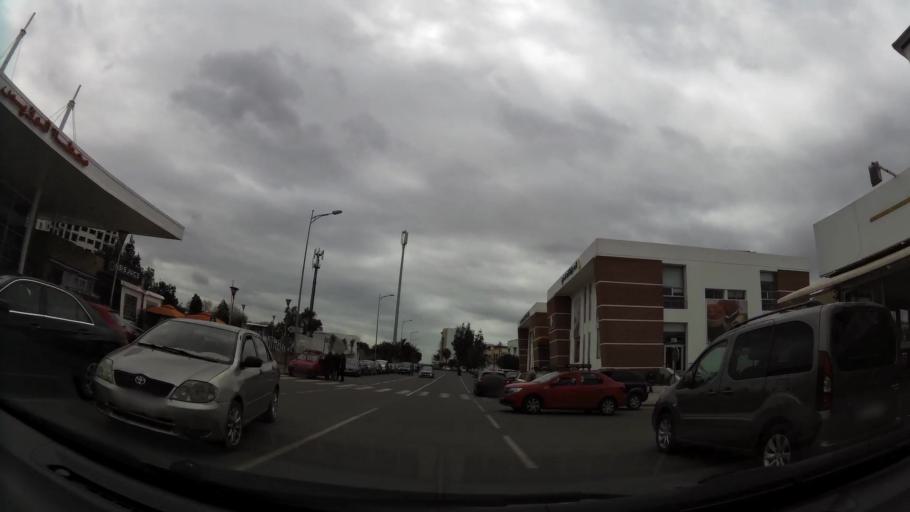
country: MA
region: Grand Casablanca
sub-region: Casablanca
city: Casablanca
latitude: 33.5549
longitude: -7.6318
